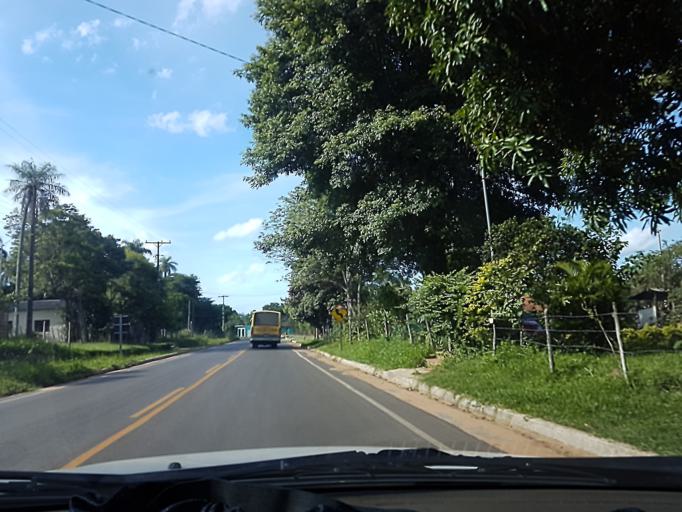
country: PY
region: Central
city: Limpio
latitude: -25.2168
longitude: -57.4473
